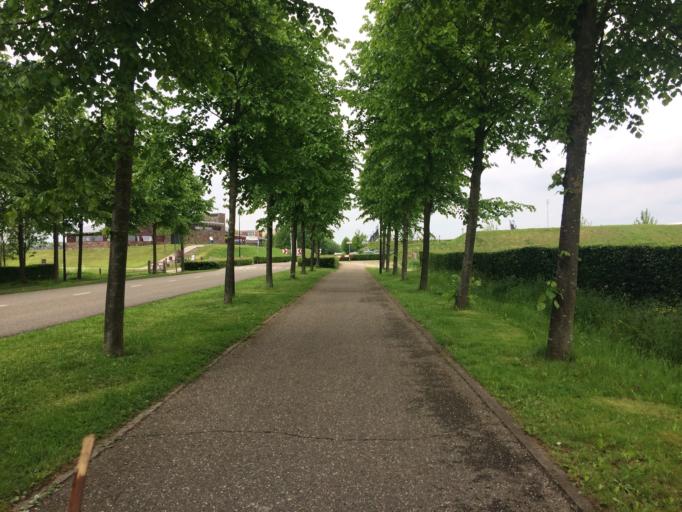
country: NL
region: Gelderland
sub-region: Gemeente Maasdriel
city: Hedel
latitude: 51.7243
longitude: 5.2570
